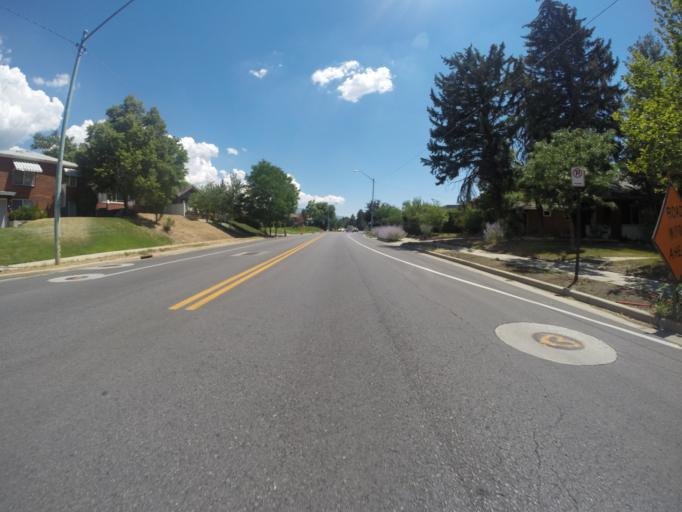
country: US
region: Utah
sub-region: Salt Lake County
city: Willard
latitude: 40.7145
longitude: -111.8559
